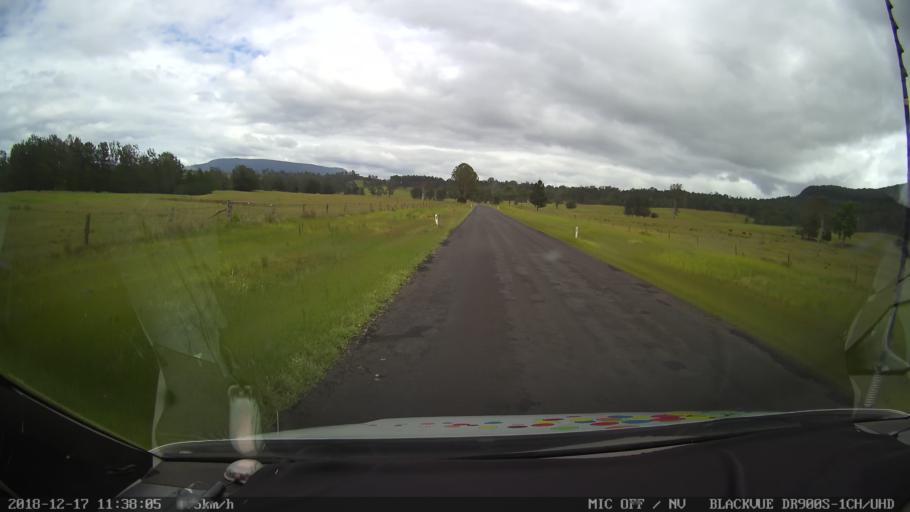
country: AU
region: New South Wales
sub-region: Kyogle
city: Kyogle
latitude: -28.6990
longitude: 152.6023
